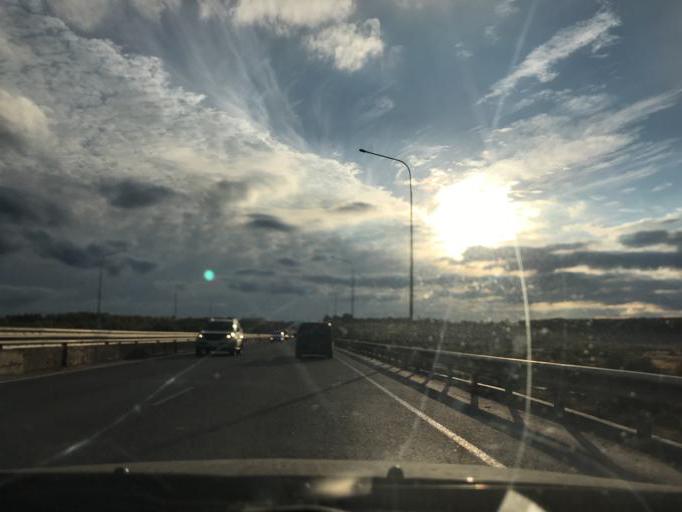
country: RU
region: Kaluga
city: Kurovskoye
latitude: 54.5496
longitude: 36.0226
